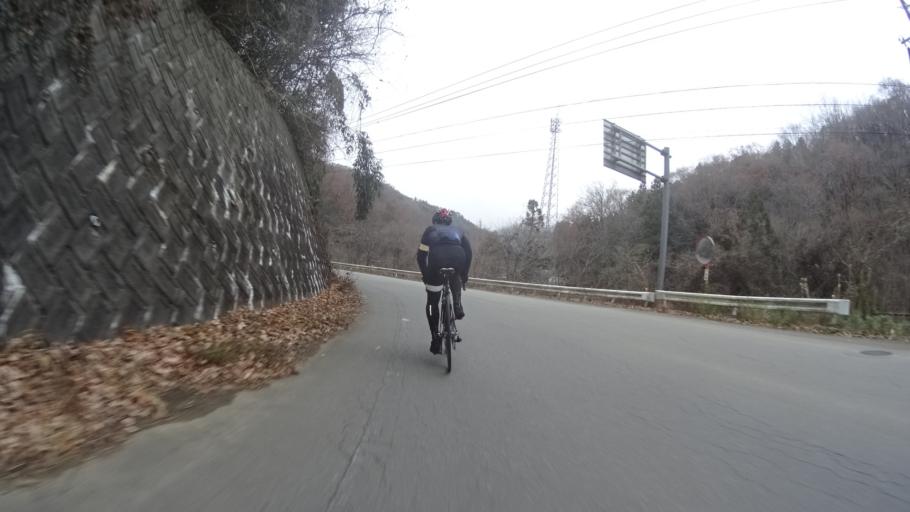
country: JP
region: Yamanashi
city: Uenohara
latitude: 35.6308
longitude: 139.1237
